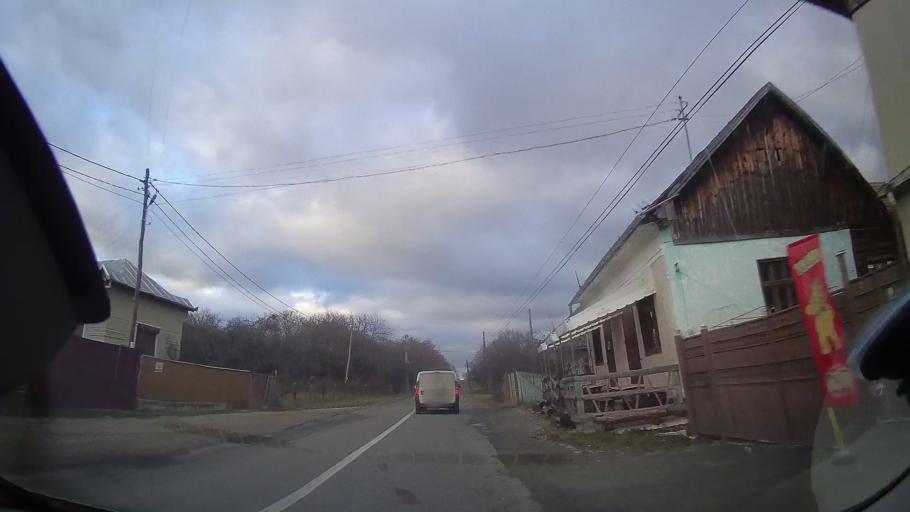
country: RO
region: Cluj
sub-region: Comuna Sancraiu
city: Sancraiu
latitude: 46.8000
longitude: 22.9949
